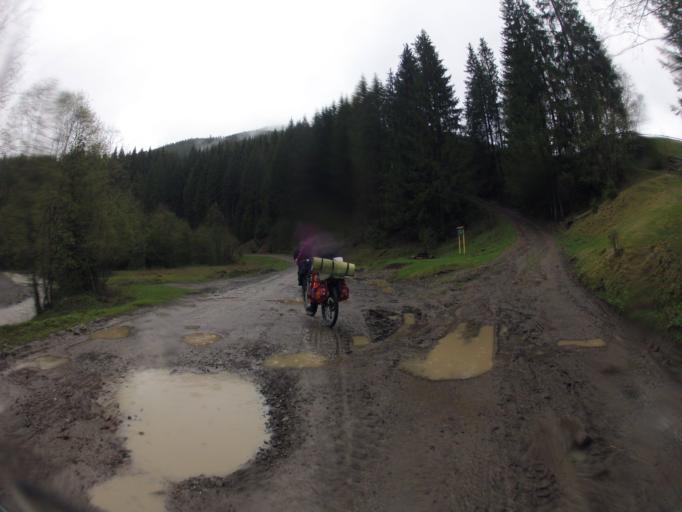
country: RO
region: Suceava
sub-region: Comuna Izvoarele Sucevei
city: Izvoarele Sucevei
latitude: 47.8340
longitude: 25.0481
